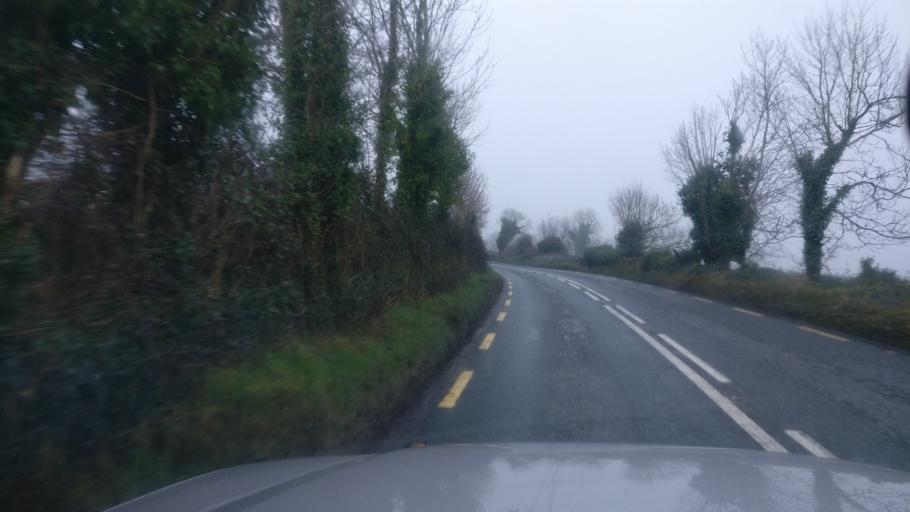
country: IE
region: Connaught
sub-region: County Galway
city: Loughrea
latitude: 53.1919
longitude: -8.5954
